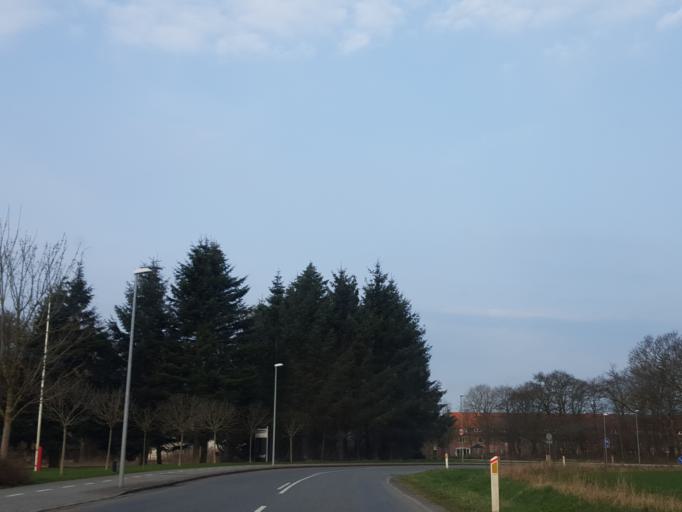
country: DK
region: South Denmark
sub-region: Esbjerg Kommune
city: Bramming
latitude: 55.4852
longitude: 8.7005
